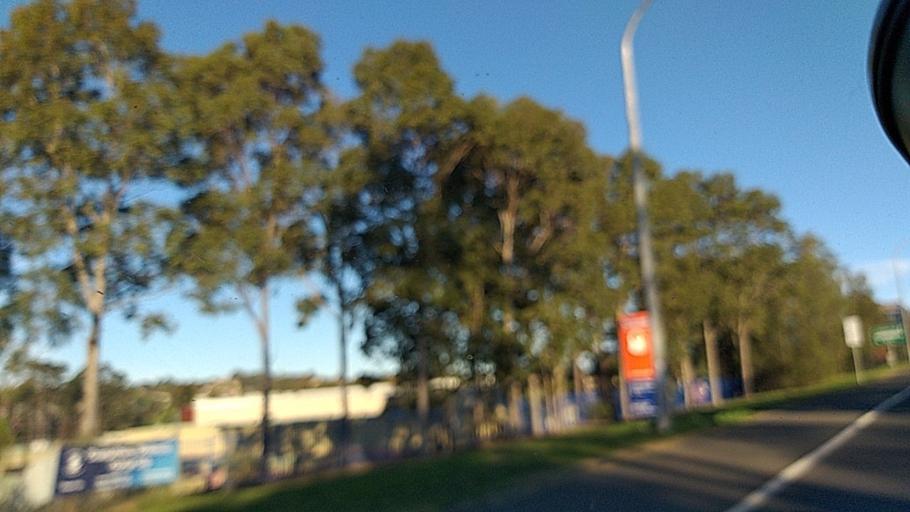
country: AU
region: New South Wales
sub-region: Campbelltown Municipality
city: Leumeah
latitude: -34.0425
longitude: 150.8294
